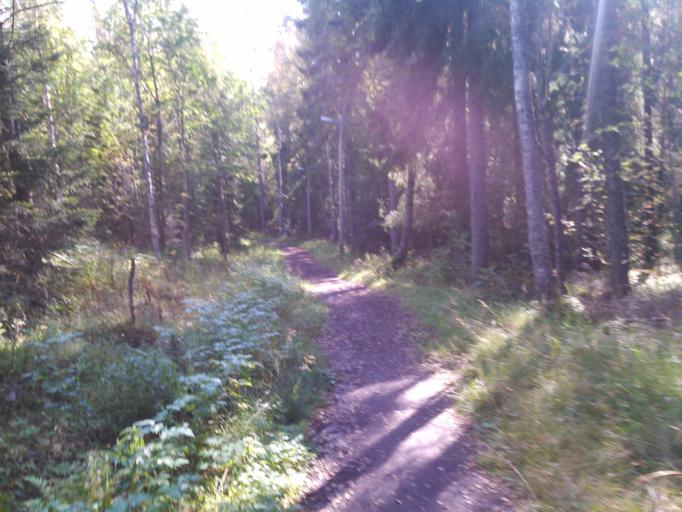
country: SE
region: Vaesterbotten
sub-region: Umea Kommun
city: Umea
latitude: 63.7940
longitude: 20.3167
